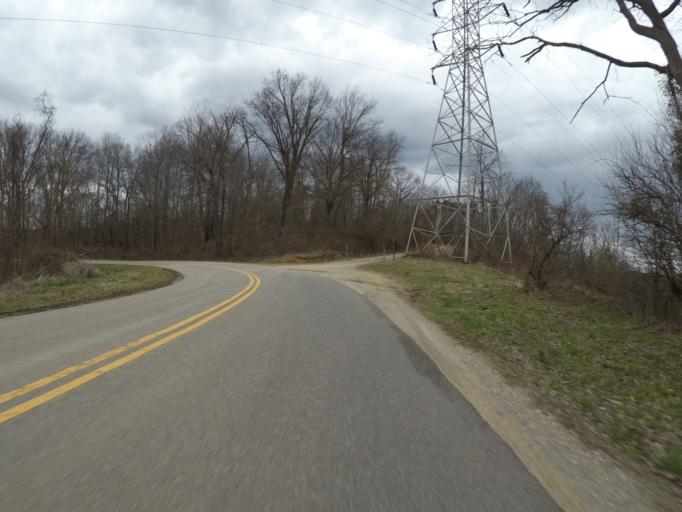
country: US
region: Ohio
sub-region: Lawrence County
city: Burlington
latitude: 38.4500
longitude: -82.5244
